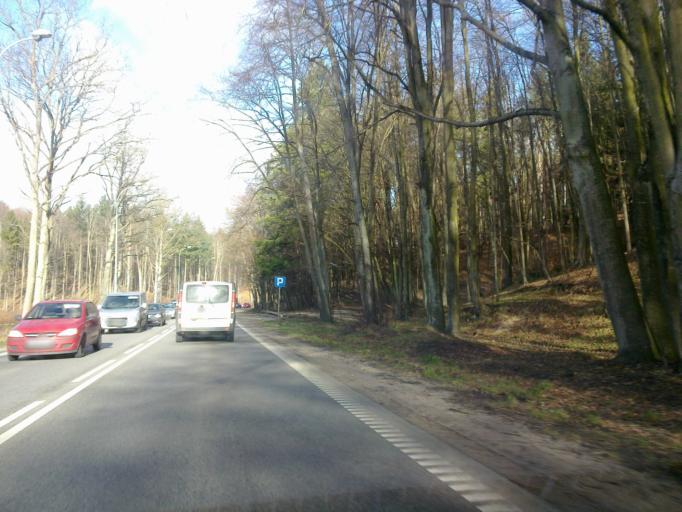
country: PL
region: Pomeranian Voivodeship
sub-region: Gdynia
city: Wielki Kack
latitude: 54.4226
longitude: 18.5083
